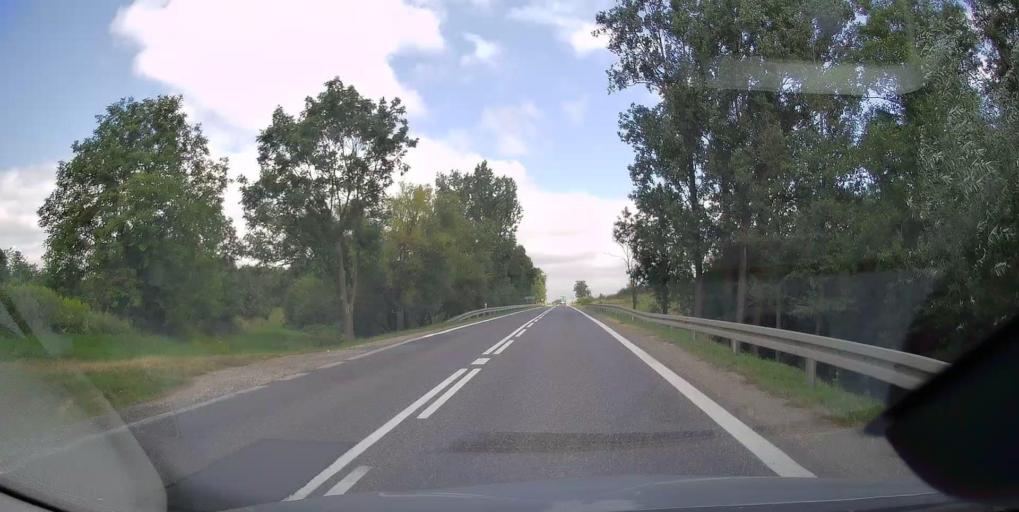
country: PL
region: Swietokrzyskie
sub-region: Powiat sandomierski
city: Klimontow
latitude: 50.6117
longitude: 21.4707
